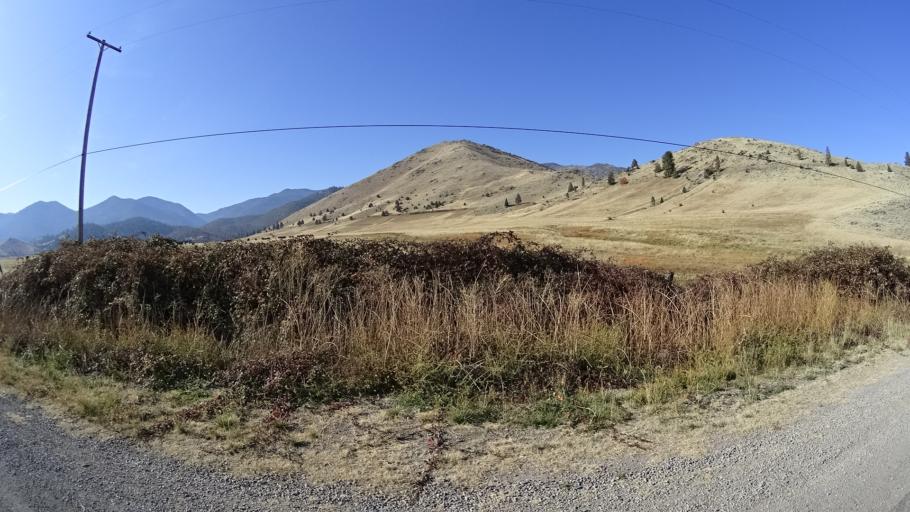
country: US
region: California
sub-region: Siskiyou County
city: Weed
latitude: 41.4635
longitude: -122.4647
